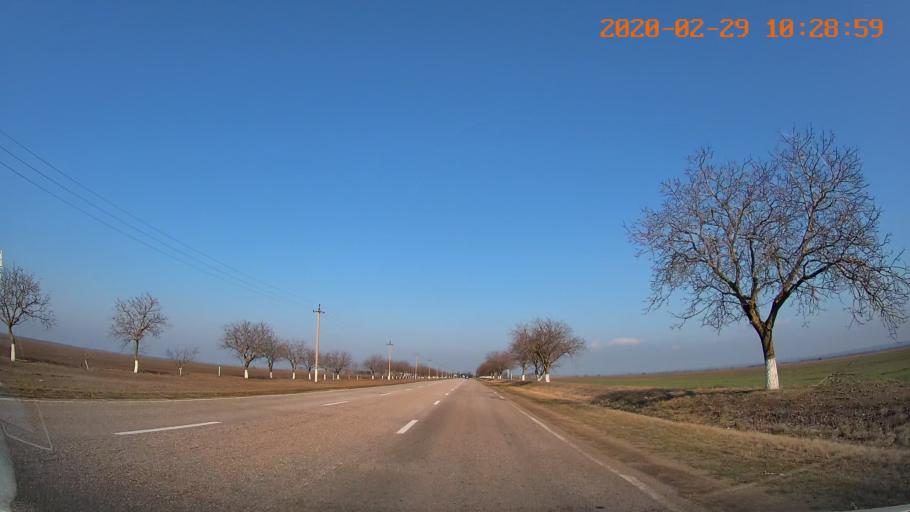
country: MD
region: Telenesti
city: Tiraspolul Nou
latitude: 46.9180
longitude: 29.5882
